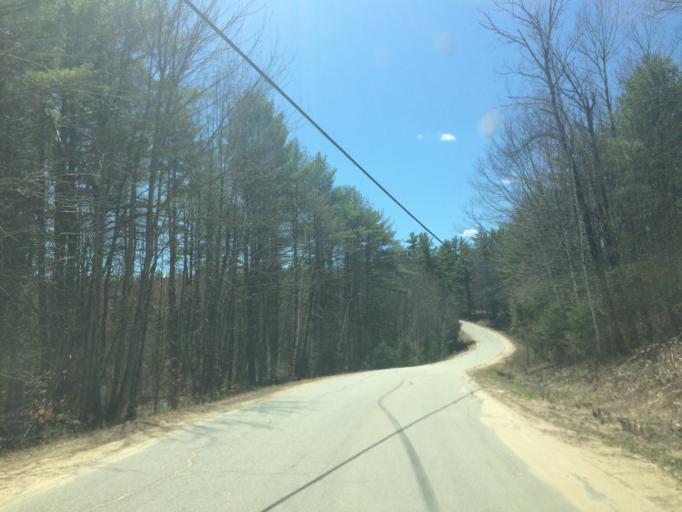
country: US
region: Maine
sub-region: York County
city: Cornish
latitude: 43.7757
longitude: -70.8649
